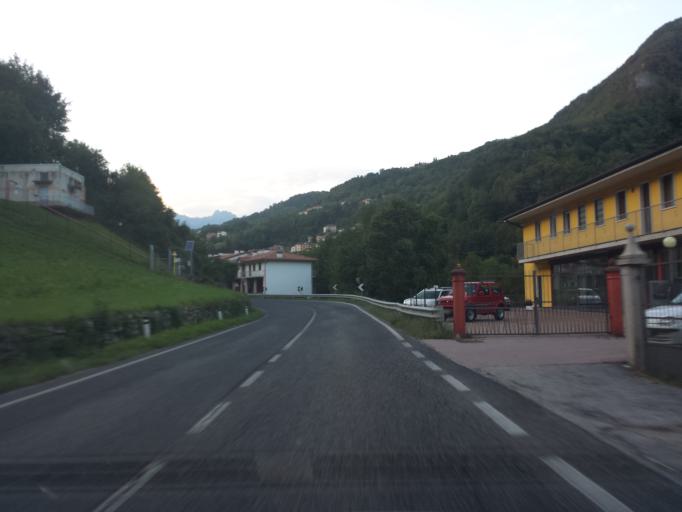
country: IT
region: Veneto
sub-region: Provincia di Vicenza
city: San Quirico
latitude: 45.6841
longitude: 11.2696
